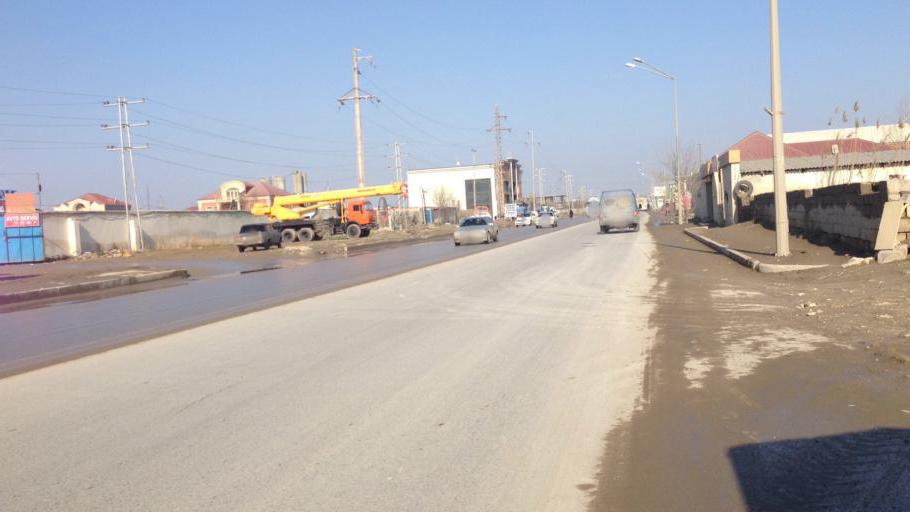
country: AZ
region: Baki
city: Binagadi
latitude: 40.4462
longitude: 49.8441
